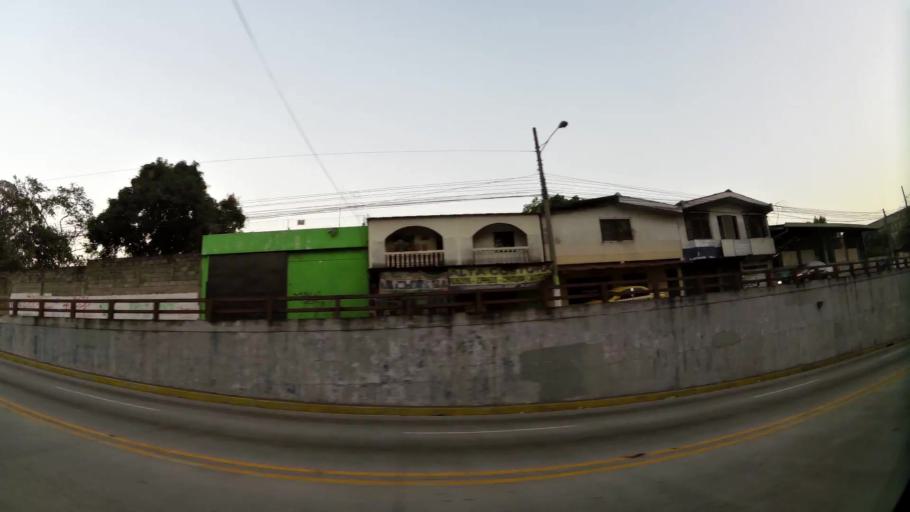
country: SV
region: San Salvador
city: Mejicanos
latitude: 13.7088
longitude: -89.2264
